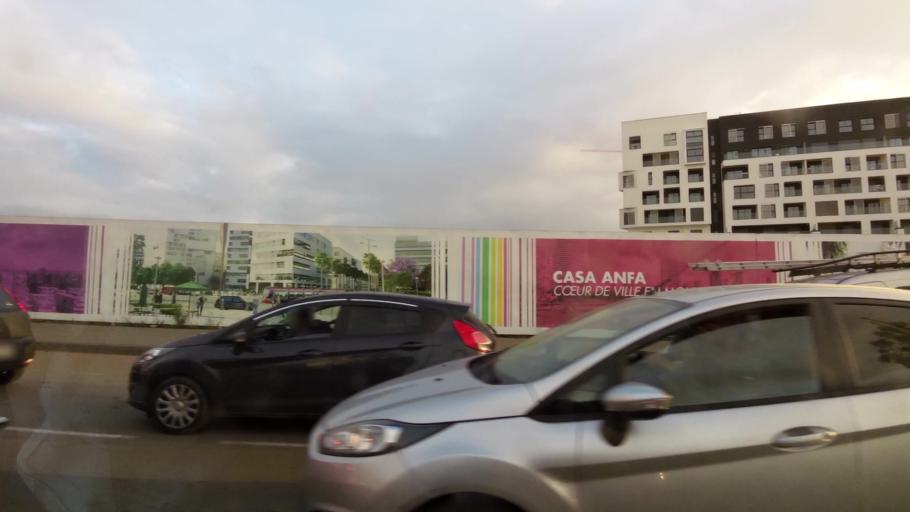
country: MA
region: Grand Casablanca
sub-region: Casablanca
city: Casablanca
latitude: 33.5671
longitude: -7.6580
